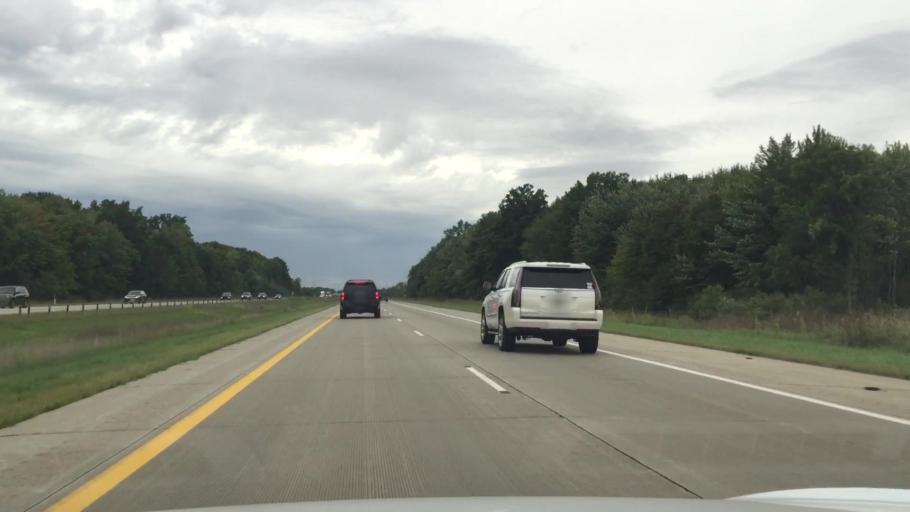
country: US
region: Michigan
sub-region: Macomb County
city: Richmond
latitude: 42.7625
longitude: -82.6952
